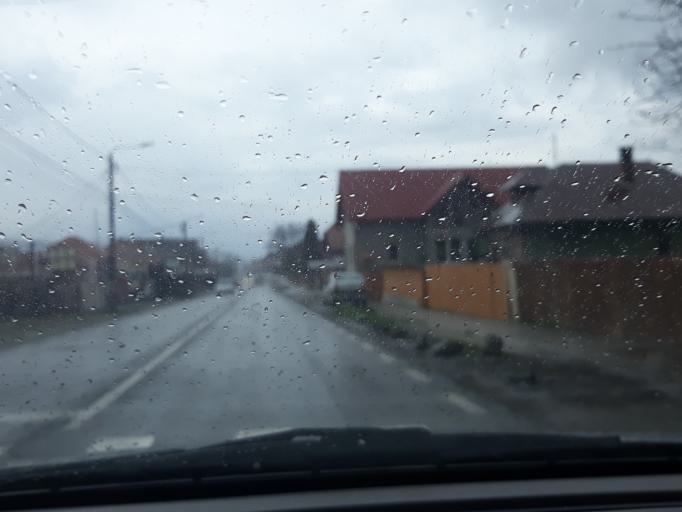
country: RO
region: Harghita
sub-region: Comuna Corund
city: Corund
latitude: 46.4750
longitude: 25.1775
